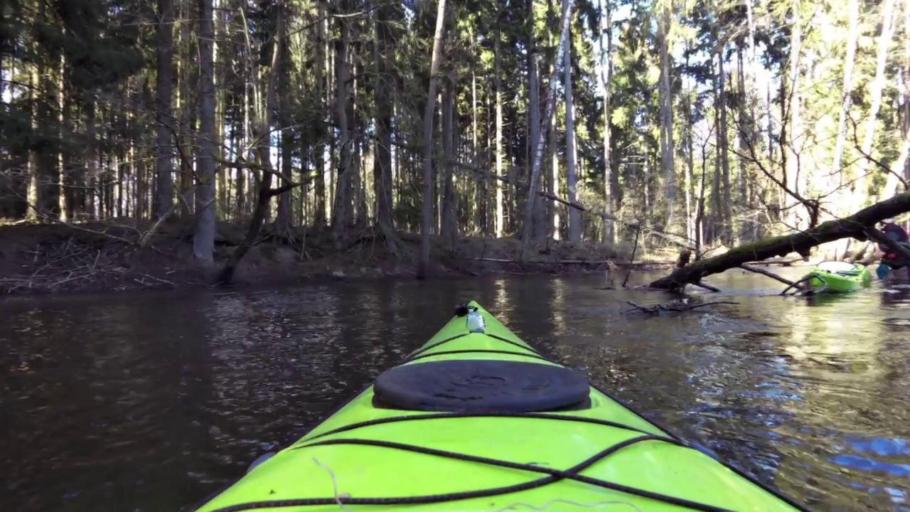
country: PL
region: West Pomeranian Voivodeship
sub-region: Powiat lobeski
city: Lobez
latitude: 53.7096
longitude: 15.5469
